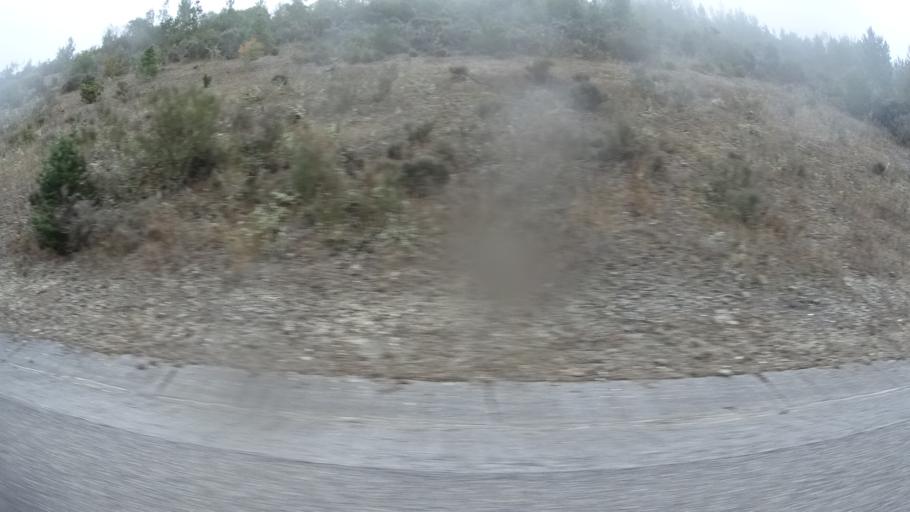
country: ES
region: Galicia
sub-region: Provincia de Lugo
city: Becerrea
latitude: 42.8302
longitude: -7.1179
